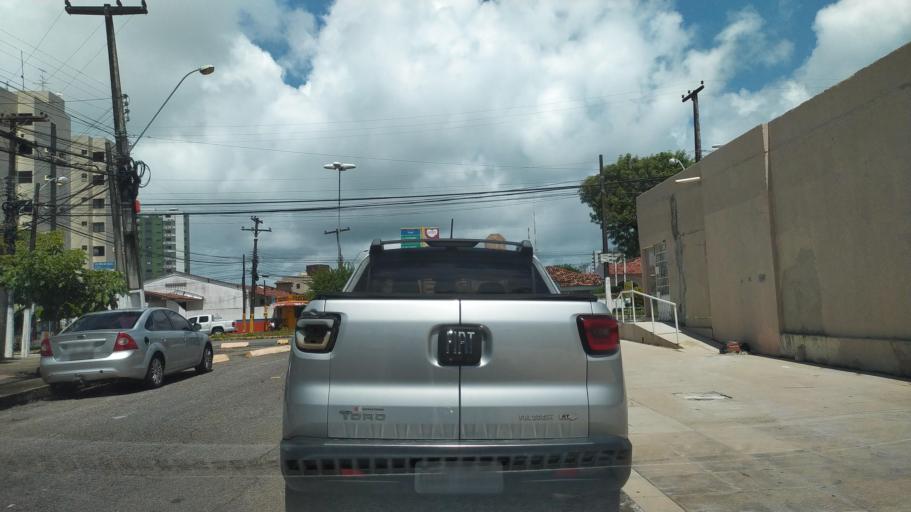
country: BR
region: Alagoas
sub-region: Maceio
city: Maceio
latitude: -9.6524
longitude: -35.7313
